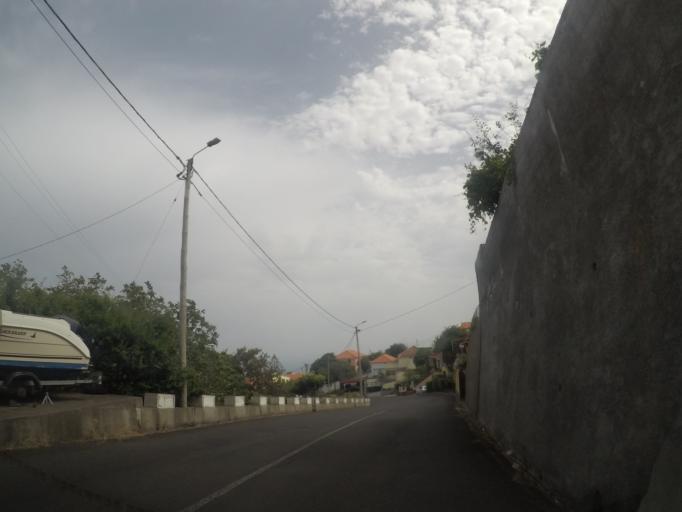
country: PT
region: Madeira
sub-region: Santa Cruz
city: Santa Cruz
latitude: 32.6737
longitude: -16.8179
